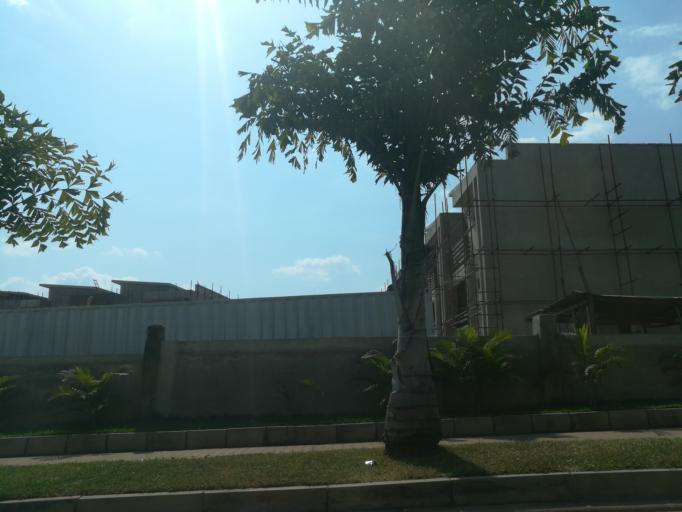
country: NG
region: Abuja Federal Capital Territory
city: Abuja
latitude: 9.0616
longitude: 7.4250
